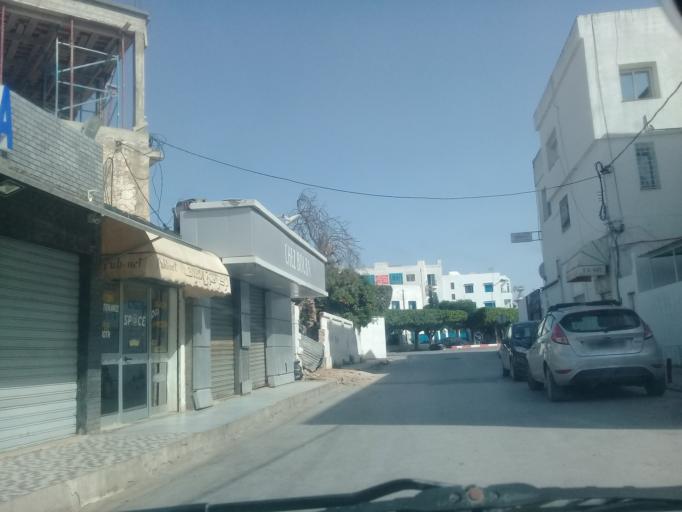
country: TN
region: Tunis
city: Al Marsa
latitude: 36.8815
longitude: 10.3267
